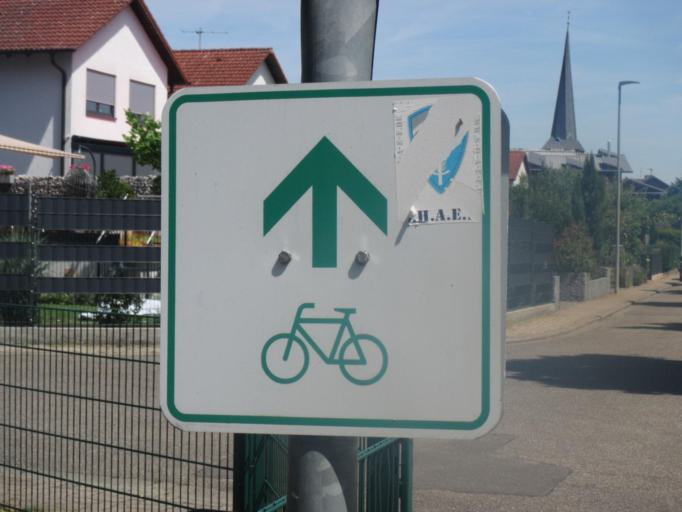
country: DE
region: Rheinland-Pfalz
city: Siebeldingen
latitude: 49.2099
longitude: 8.0475
